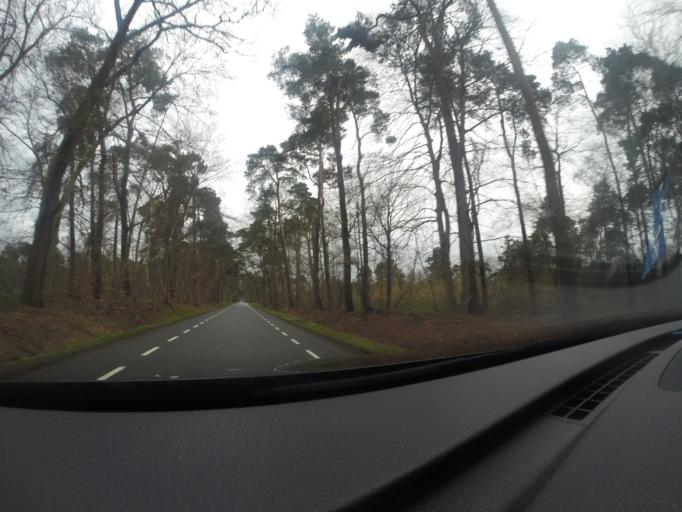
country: NL
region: Overijssel
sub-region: Gemeente Hof van Twente
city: Delden
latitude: 52.2430
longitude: 6.7256
